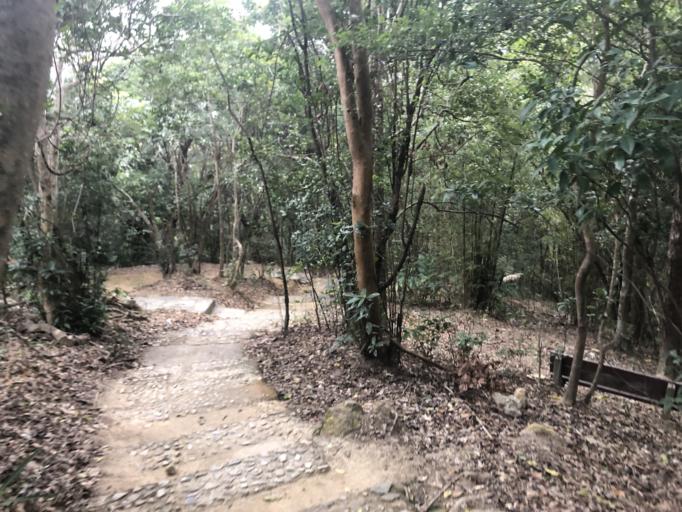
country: HK
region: Wanchai
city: Wan Chai
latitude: 22.2800
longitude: 114.2094
